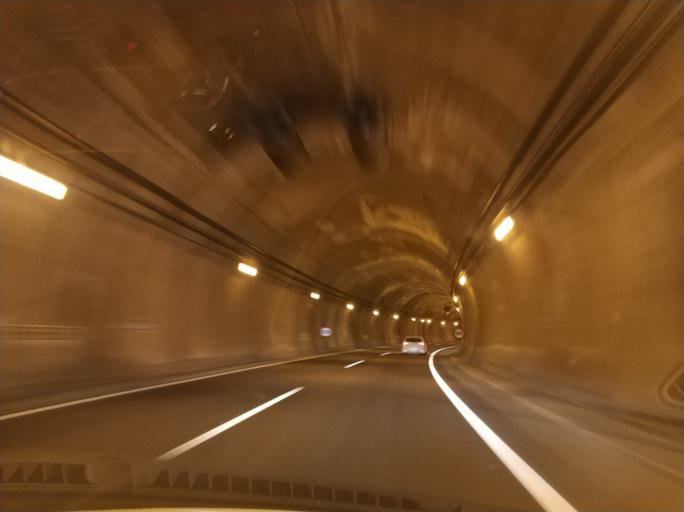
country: ES
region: Castille and Leon
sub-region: Provincia de Leon
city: Soto y Amio
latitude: 42.8605
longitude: -5.8737
